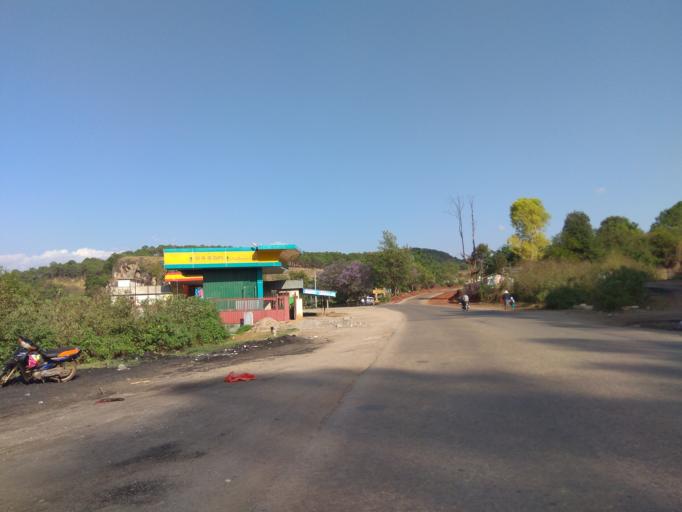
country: MM
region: Shan
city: Taunggyi
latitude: 20.6440
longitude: 96.6058
